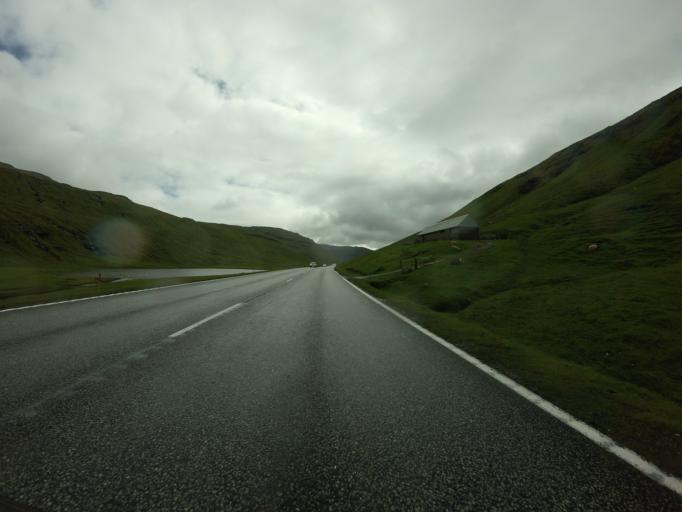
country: FO
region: Streymoy
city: Kollafjordhur
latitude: 62.1257
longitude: -6.9990
